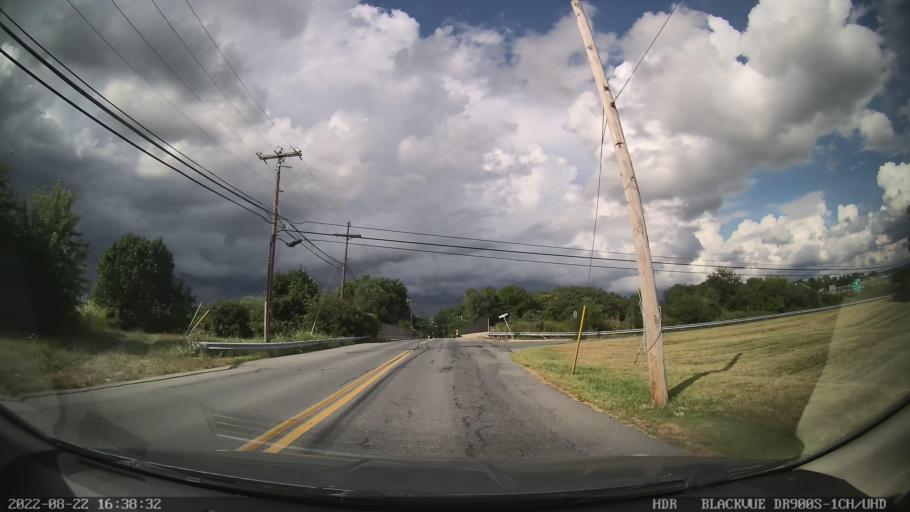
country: US
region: Pennsylvania
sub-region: Lehigh County
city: Dorneyville
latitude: 40.5692
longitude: -75.5351
